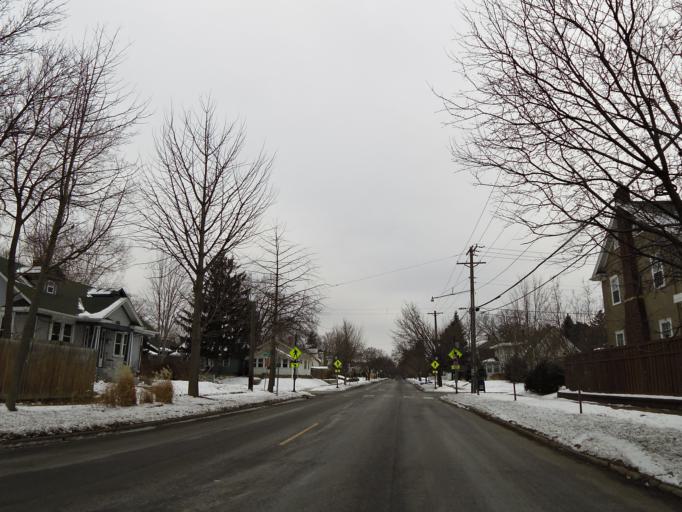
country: US
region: Minnesota
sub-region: Ramsey County
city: Falcon Heights
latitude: 44.9312
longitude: -93.1925
